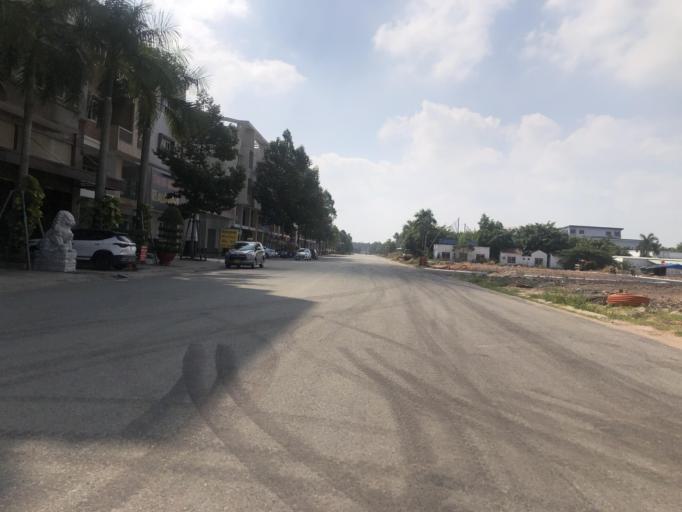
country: VN
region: Binh Duong
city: Thu Dau Mot
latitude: 11.0720
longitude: 106.6829
